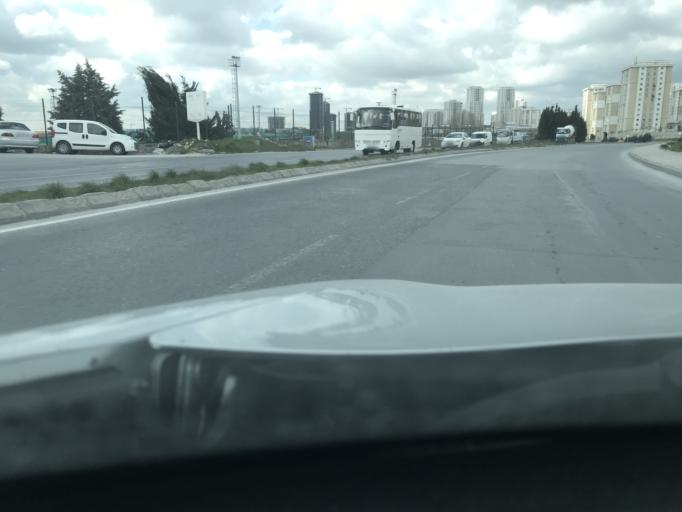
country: TR
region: Istanbul
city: Esenyurt
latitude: 41.0806
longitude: 28.6530
